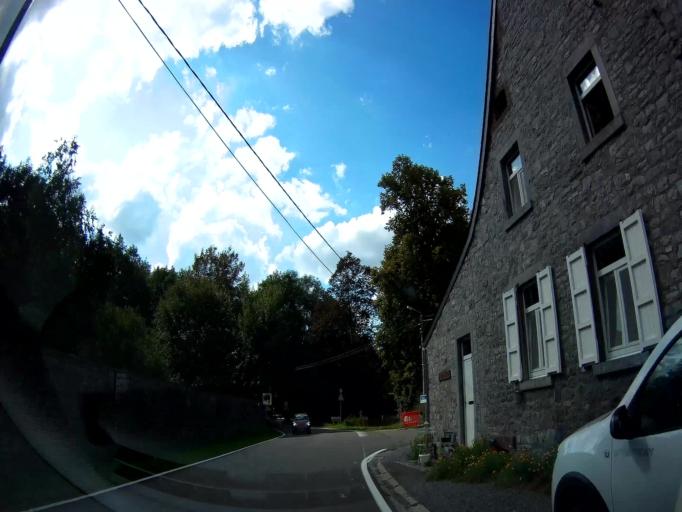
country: BE
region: Wallonia
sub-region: Province de Namur
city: Onhaye
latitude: 50.2919
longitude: 4.8043
